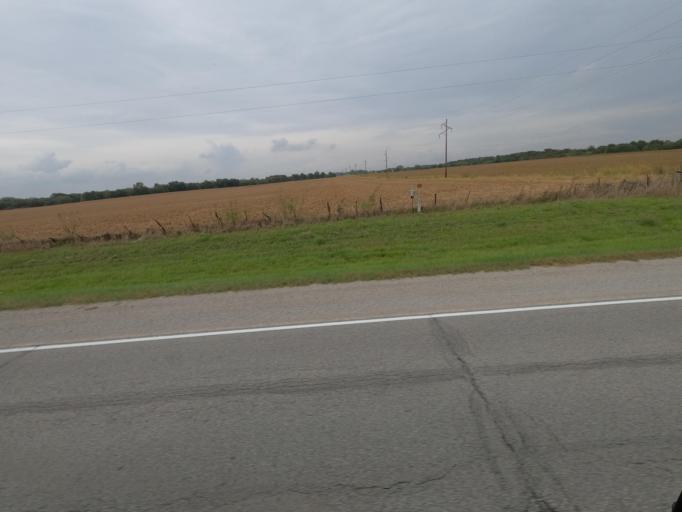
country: US
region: Iowa
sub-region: Van Buren County
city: Keosauqua
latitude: 40.8570
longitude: -92.1028
